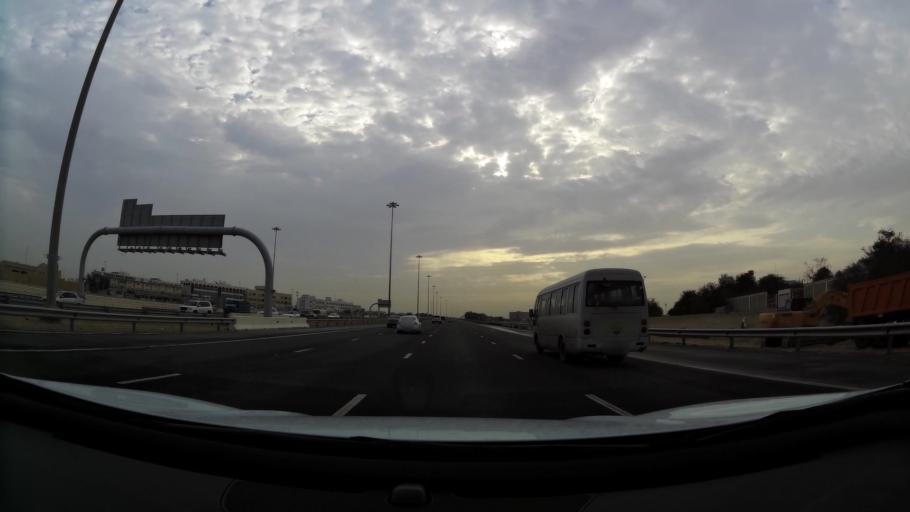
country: AE
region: Abu Dhabi
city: Abu Dhabi
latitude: 24.3054
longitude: 54.6091
